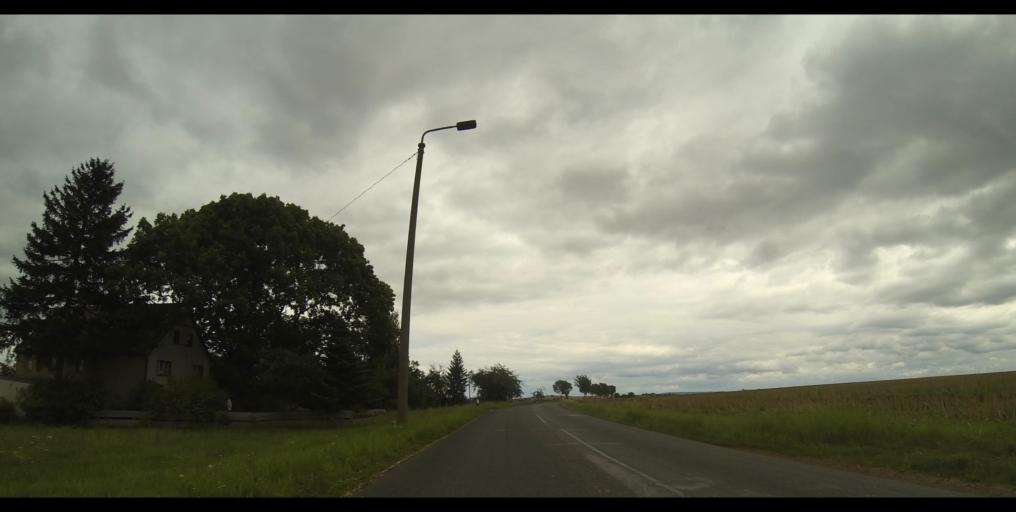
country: DE
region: Saxony
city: Reinsberg
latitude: 51.0403
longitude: 13.3626
